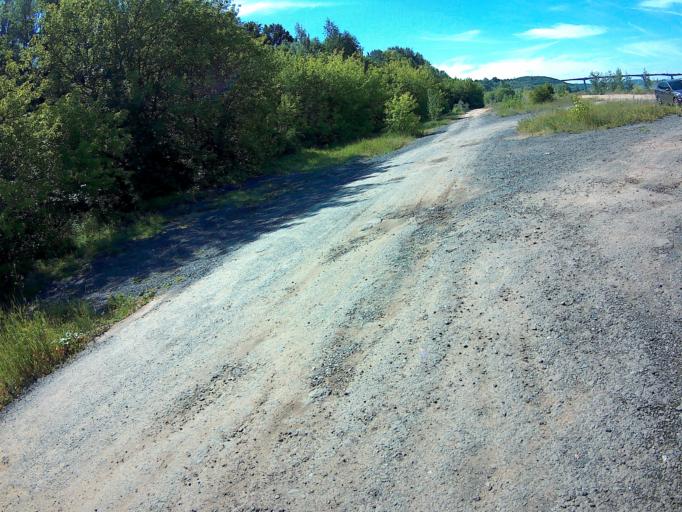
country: RU
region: Nizjnij Novgorod
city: Nizhniy Novgorod
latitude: 56.2604
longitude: 43.9667
